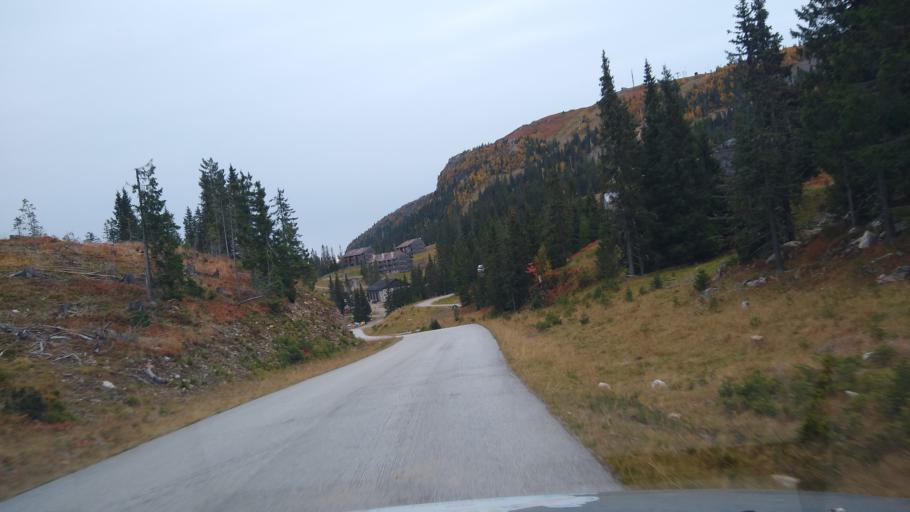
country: NO
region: Oppland
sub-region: Ringebu
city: Ringebu
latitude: 61.4758
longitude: 10.1283
